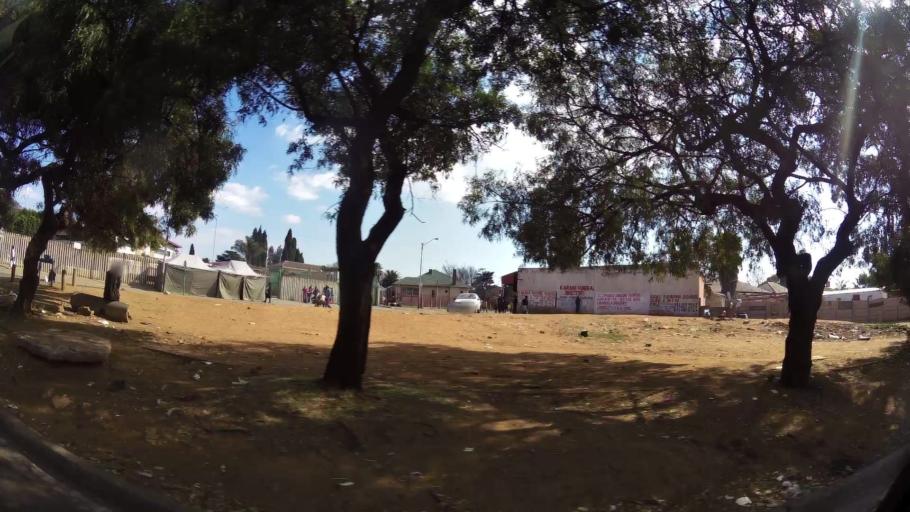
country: ZA
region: Gauteng
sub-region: Ekurhuleni Metropolitan Municipality
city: Germiston
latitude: -26.1895
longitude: 28.1688
